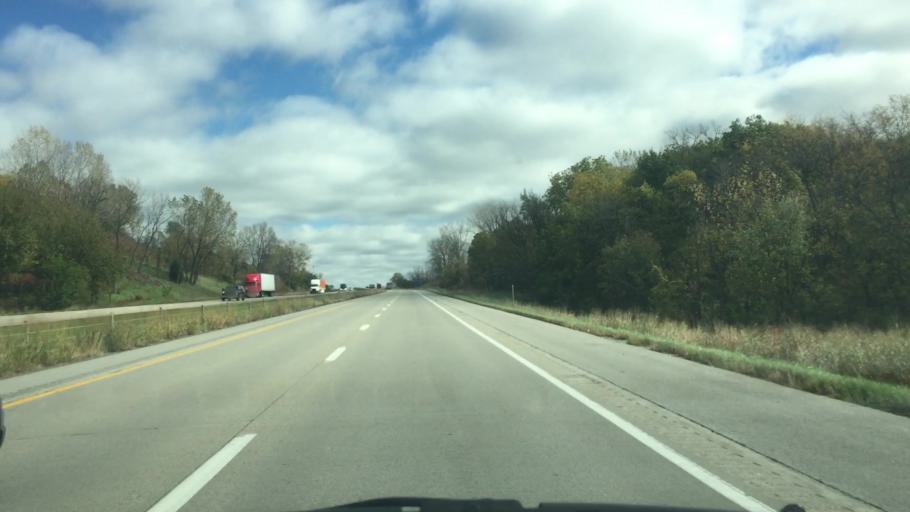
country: US
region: Iowa
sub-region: Jasper County
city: Colfax
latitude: 41.6847
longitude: -93.1591
